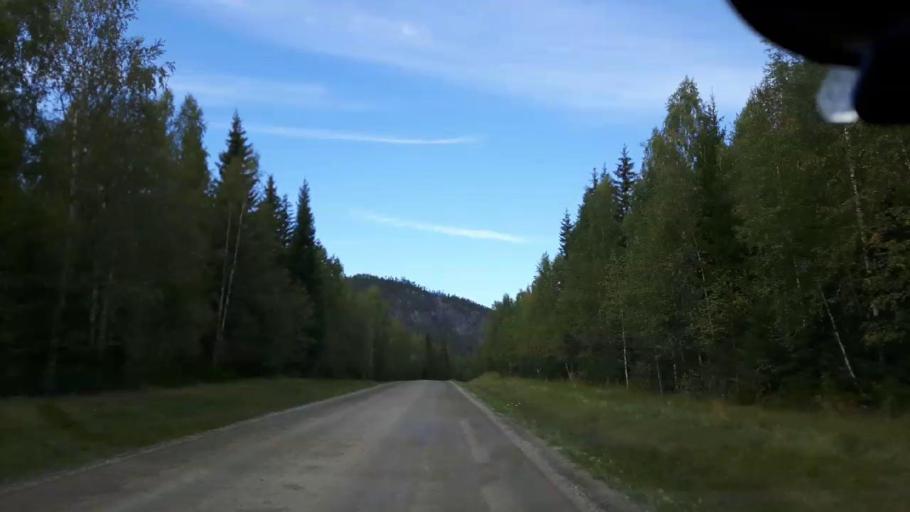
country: SE
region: Jaemtland
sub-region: Ragunda Kommun
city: Hammarstrand
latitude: 63.1226
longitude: 16.3309
